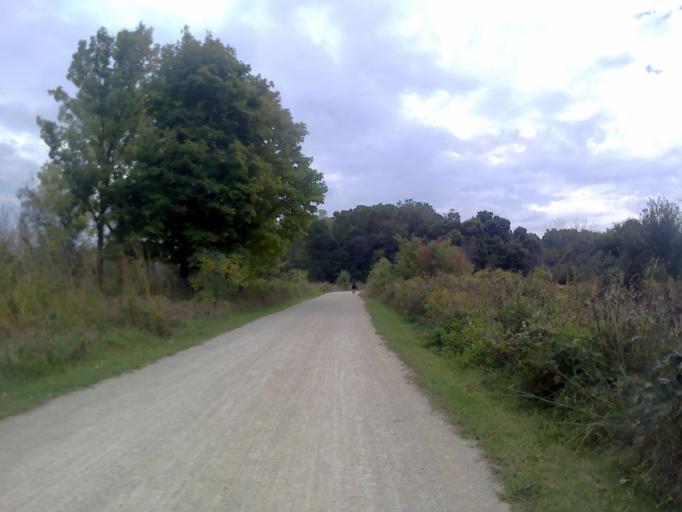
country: US
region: Illinois
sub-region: DuPage County
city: Warrenville
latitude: 41.8014
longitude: -88.1814
